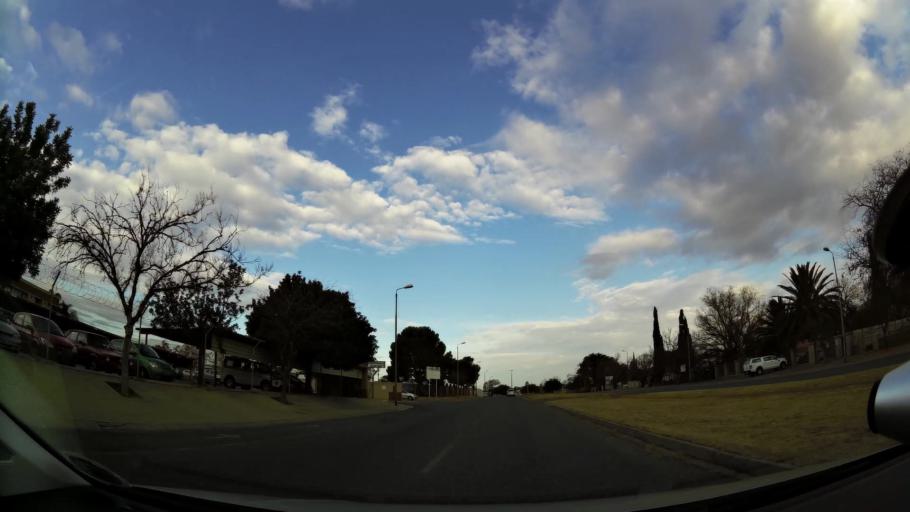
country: ZA
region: Orange Free State
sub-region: Lejweleputswa District Municipality
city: Welkom
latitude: -27.9893
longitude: 26.7296
